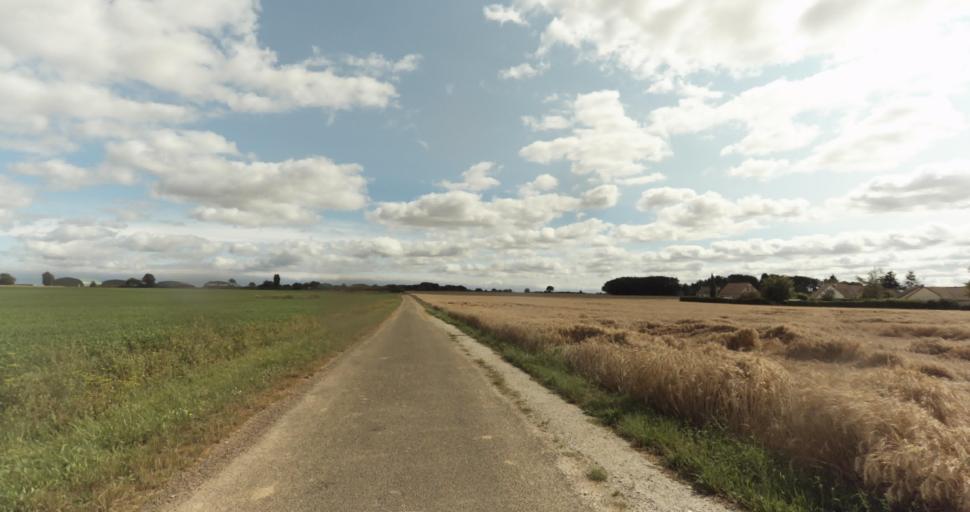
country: FR
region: Haute-Normandie
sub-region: Departement de l'Eure
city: Marcilly-sur-Eure
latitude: 48.8986
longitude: 1.2389
